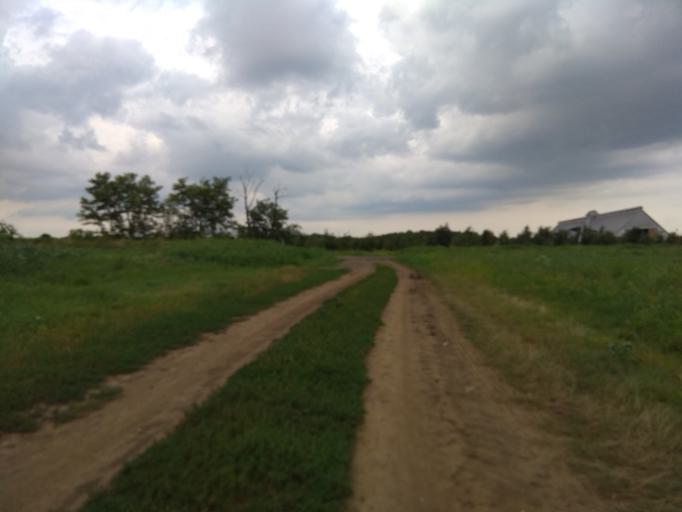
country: HU
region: Borsod-Abauj-Zemplen
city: Megyaszo
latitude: 48.1456
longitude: 21.0610
